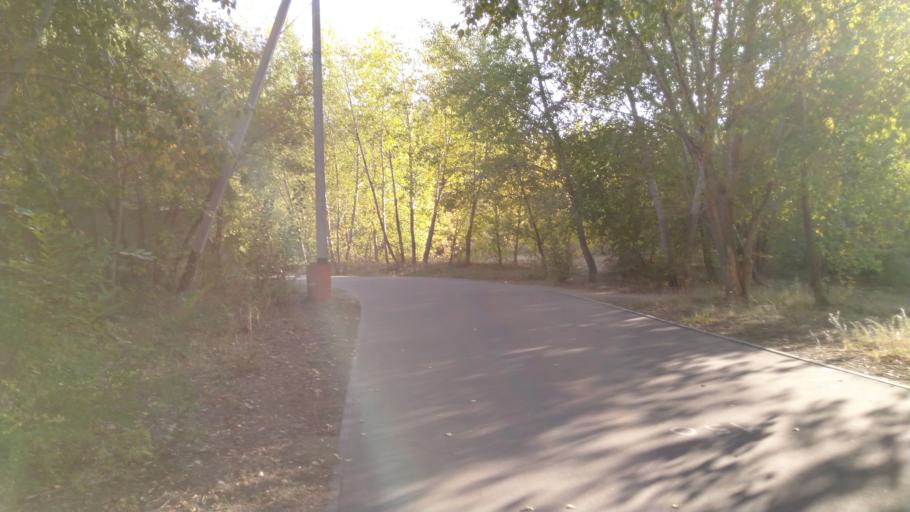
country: KZ
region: Pavlodar
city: Pavlodar
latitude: 52.2599
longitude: 76.9373
